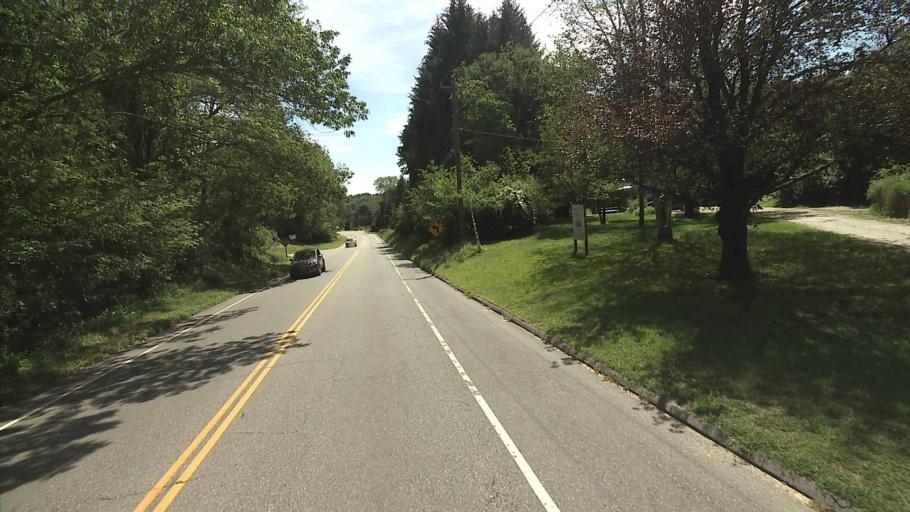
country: US
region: Connecticut
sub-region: Windham County
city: East Brooklyn
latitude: 41.8492
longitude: -71.9365
